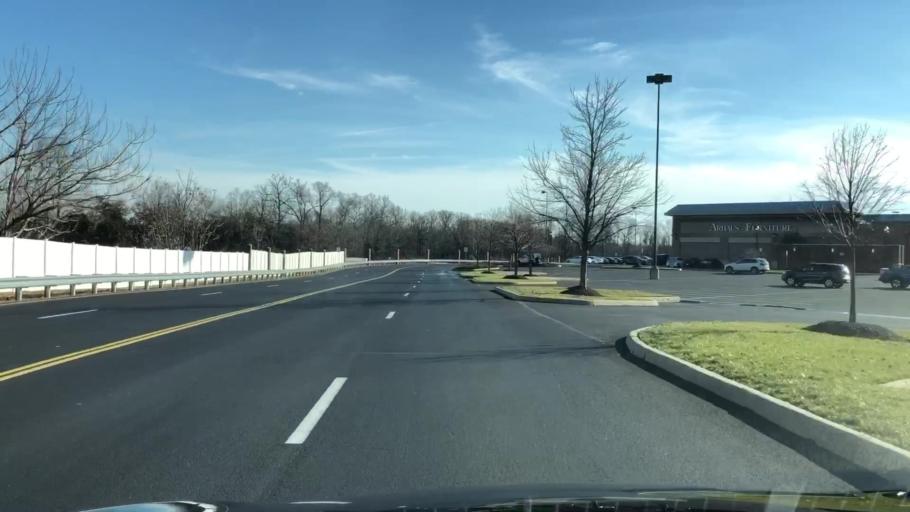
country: US
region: Virginia
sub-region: City of Fredericksburg
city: Fredericksburg
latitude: 38.2923
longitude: -77.5091
